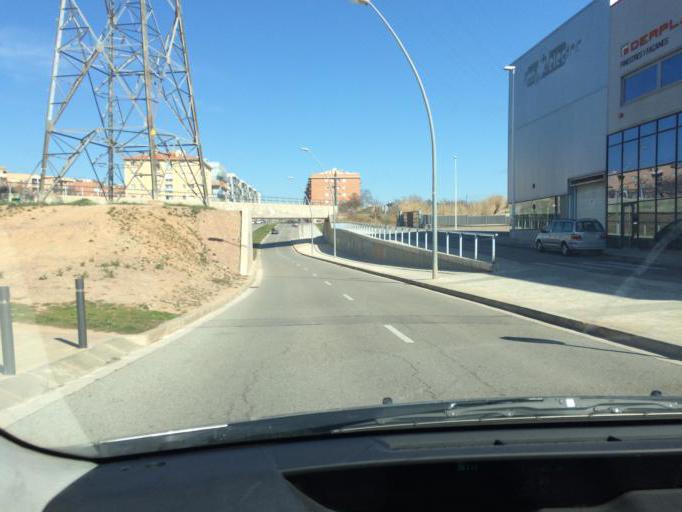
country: ES
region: Catalonia
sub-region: Provincia de Barcelona
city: Manresa
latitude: 41.7360
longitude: 1.8383
